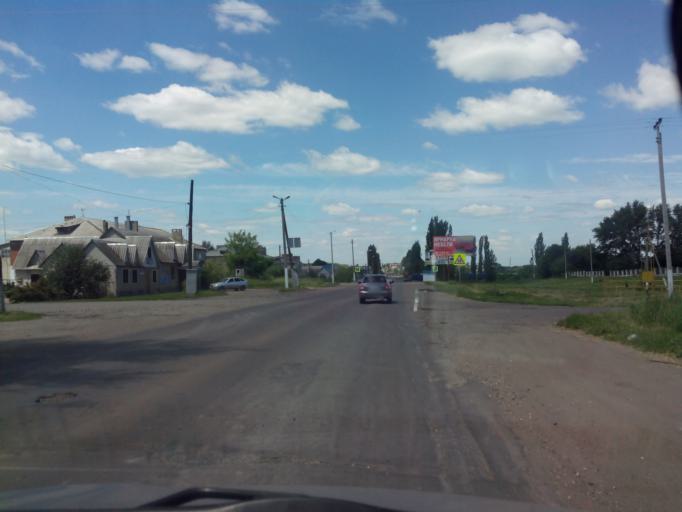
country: RU
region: Tambov
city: Zherdevka
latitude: 51.8275
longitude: 41.4945
